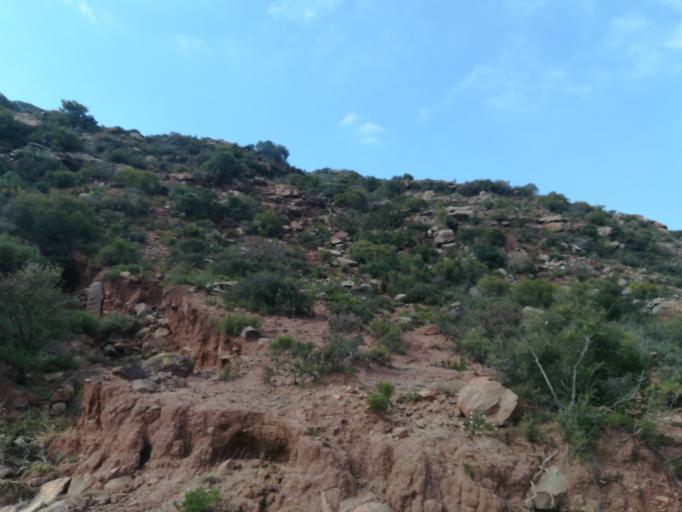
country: LS
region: Quthing
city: Quthing
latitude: -30.3386
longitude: 27.5470
